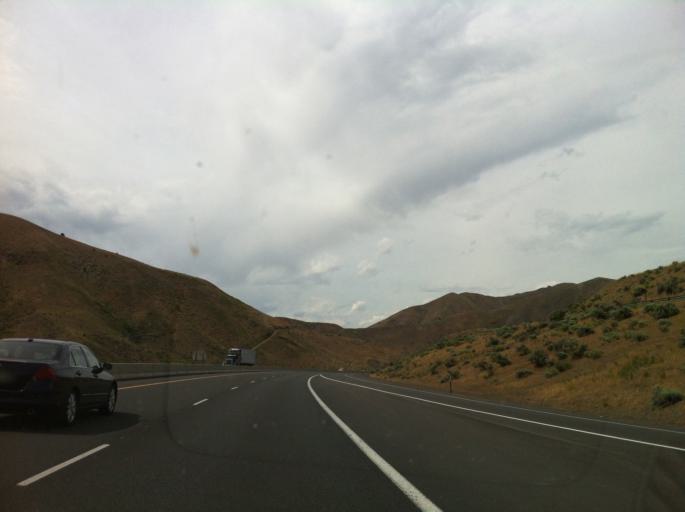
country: US
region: Idaho
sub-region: Washington County
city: Weiser
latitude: 44.4306
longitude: -117.3165
